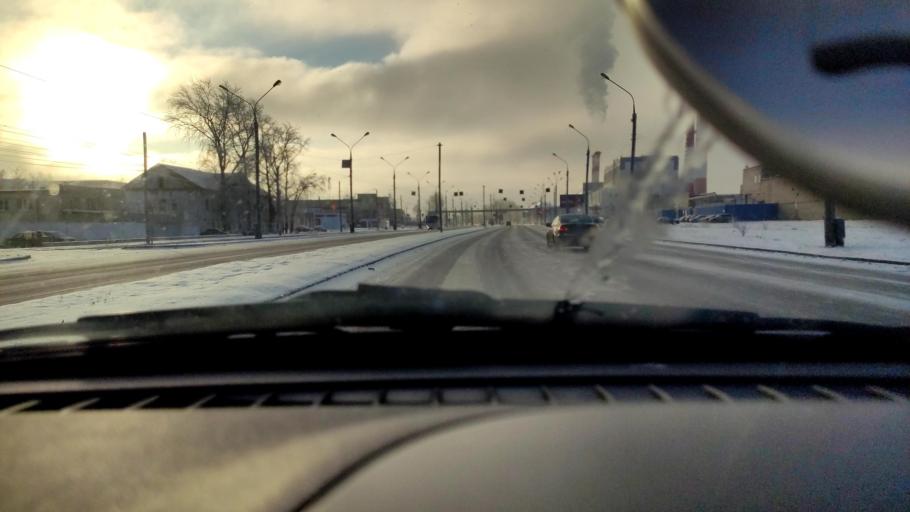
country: RU
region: Perm
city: Perm
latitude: 57.9816
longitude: 56.2605
